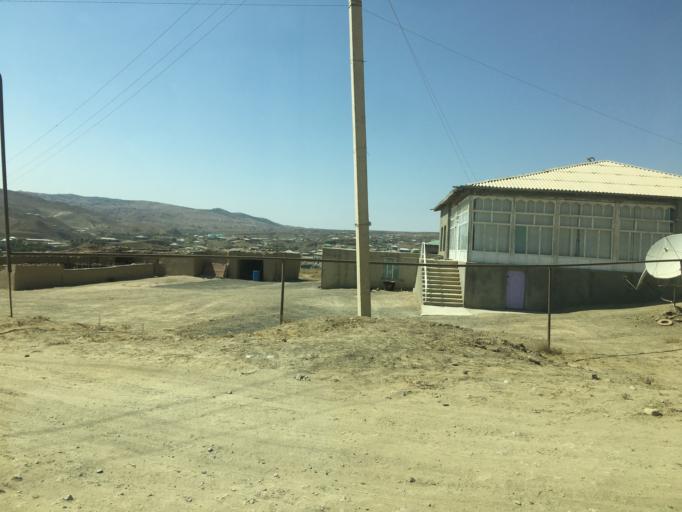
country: TM
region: Ahal
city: Baharly
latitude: 38.3910
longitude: 57.0344
